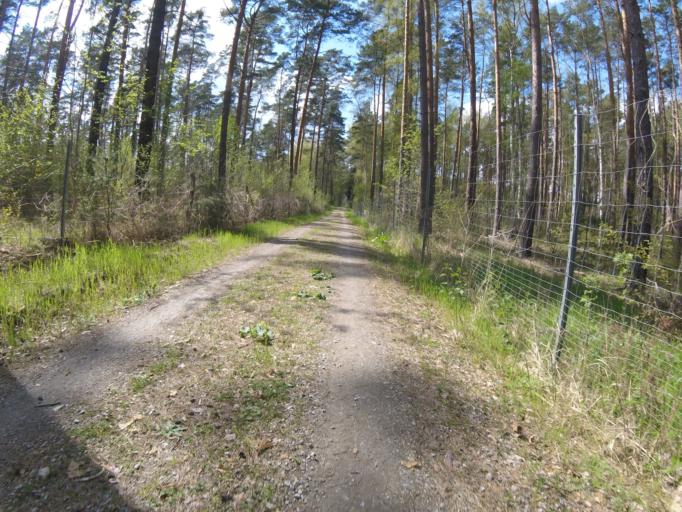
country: DE
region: Brandenburg
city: Gross Koris
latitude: 52.2115
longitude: 13.7298
